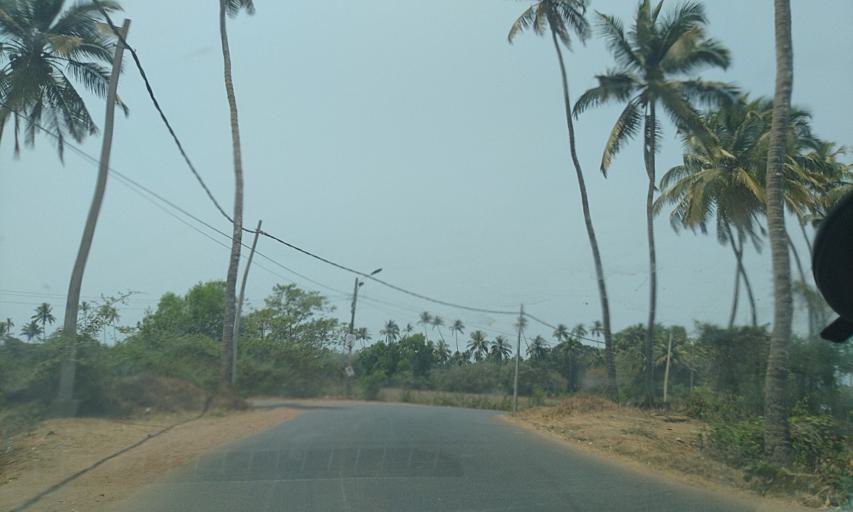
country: IN
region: Goa
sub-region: North Goa
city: Vagator
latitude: 15.5907
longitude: 73.7639
